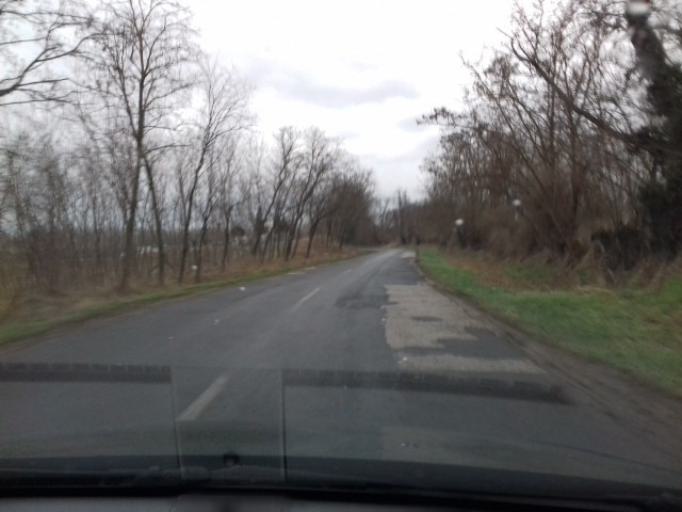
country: HU
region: Szabolcs-Szatmar-Bereg
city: Nyirbogdany
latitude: 48.0695
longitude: 21.8603
